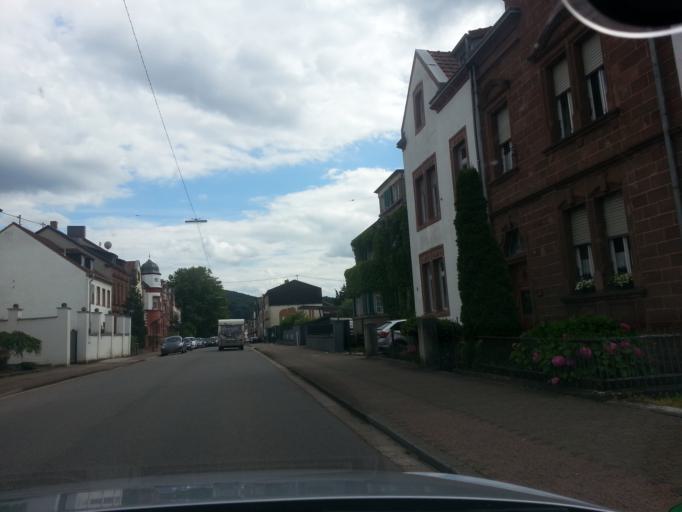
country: DE
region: Saarland
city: Merzig
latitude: 49.4505
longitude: 6.6355
